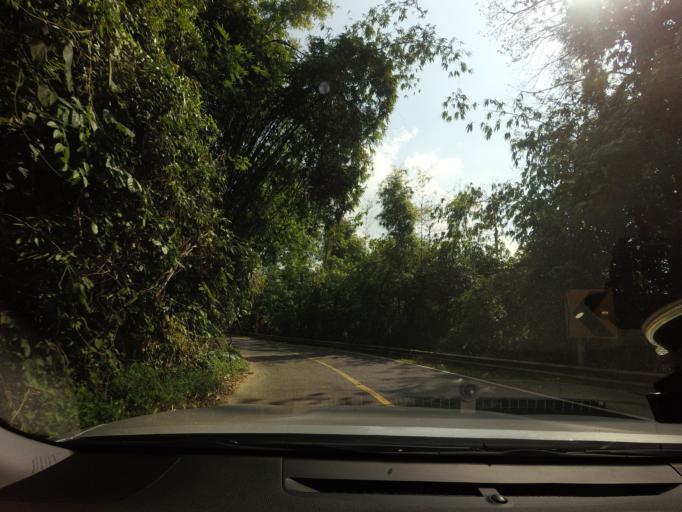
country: TH
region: Phangnga
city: Thap Put
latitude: 8.5366
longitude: 98.5628
